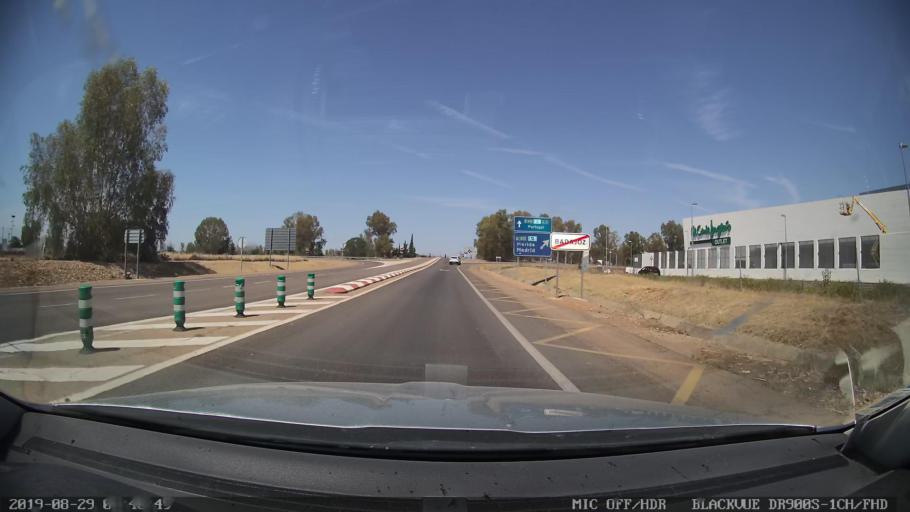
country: ES
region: Extremadura
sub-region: Provincia de Badajoz
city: Badajoz
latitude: 38.8836
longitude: -7.0249
